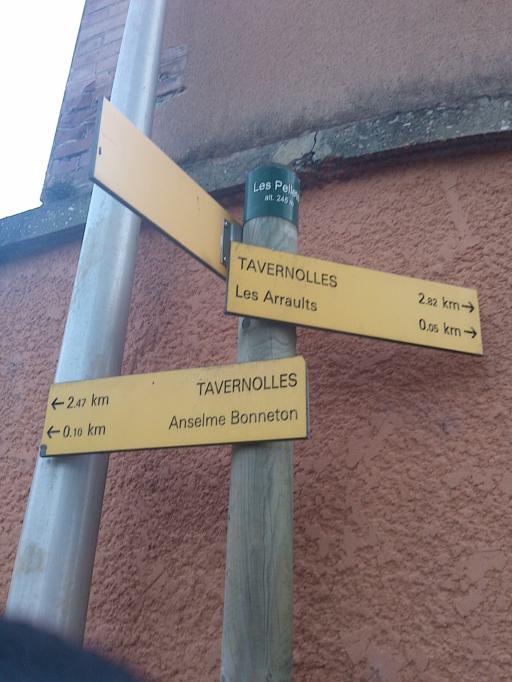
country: FR
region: Rhone-Alpes
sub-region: Departement de l'Isere
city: Eybens
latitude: 45.1466
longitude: 5.7524
